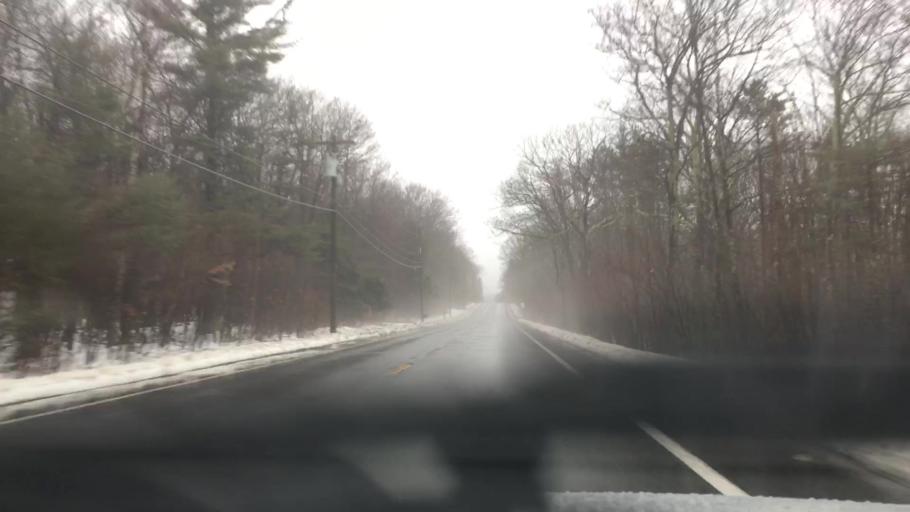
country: US
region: Massachusetts
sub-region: Hampshire County
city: Pelham
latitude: 42.3847
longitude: -72.4017
